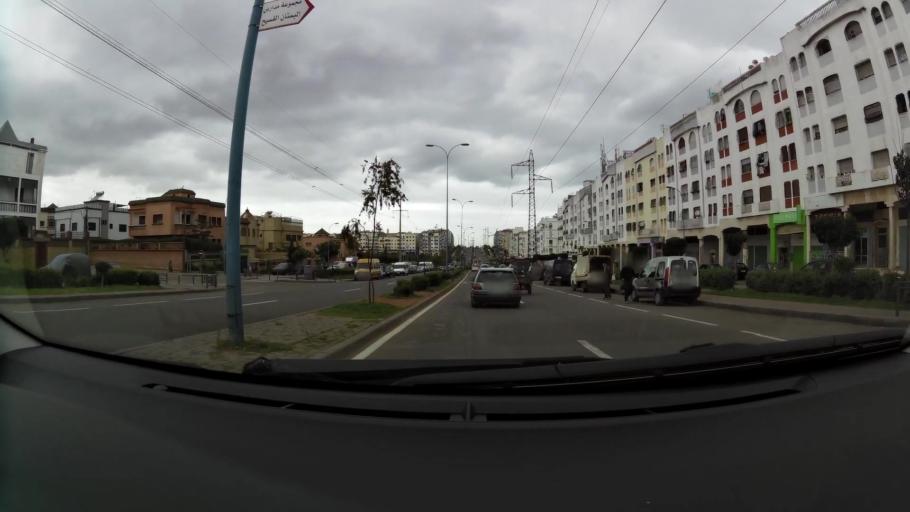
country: MA
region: Grand Casablanca
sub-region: Mediouna
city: Tit Mellil
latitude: 33.5665
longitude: -7.5308
